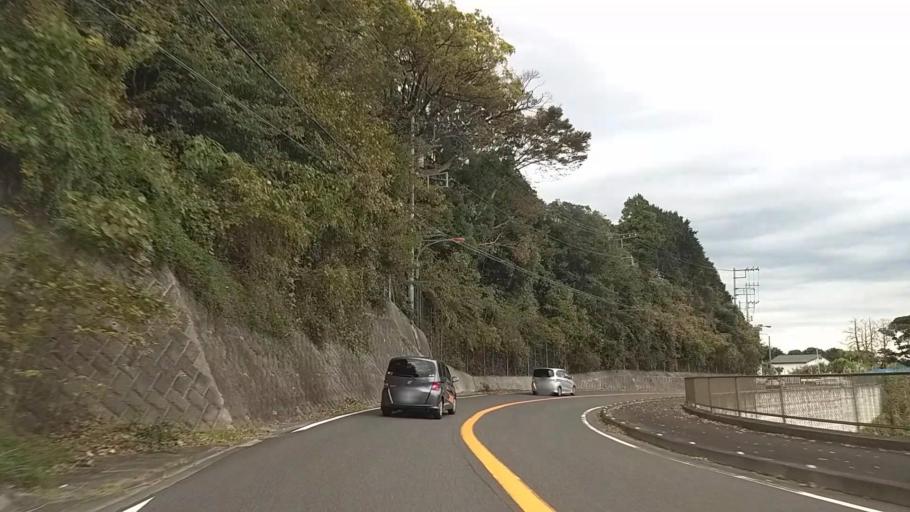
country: JP
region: Kanagawa
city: Odawara
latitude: 35.1951
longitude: 139.1341
